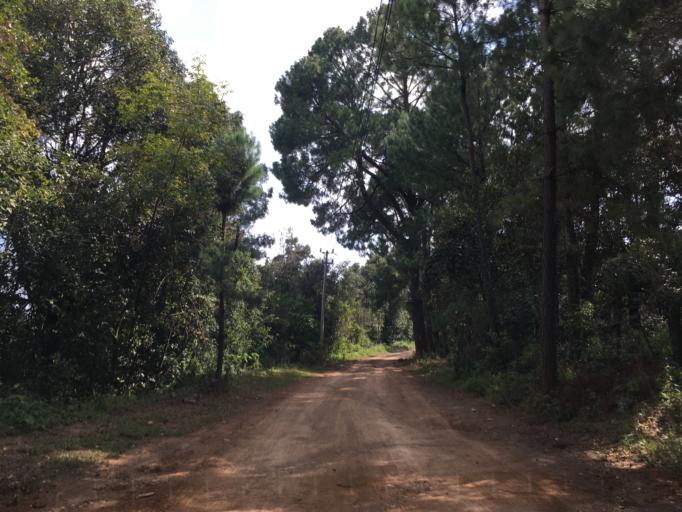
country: MX
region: Michoacan
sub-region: Morelia
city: Morelos
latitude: 19.5281
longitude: -101.2061
